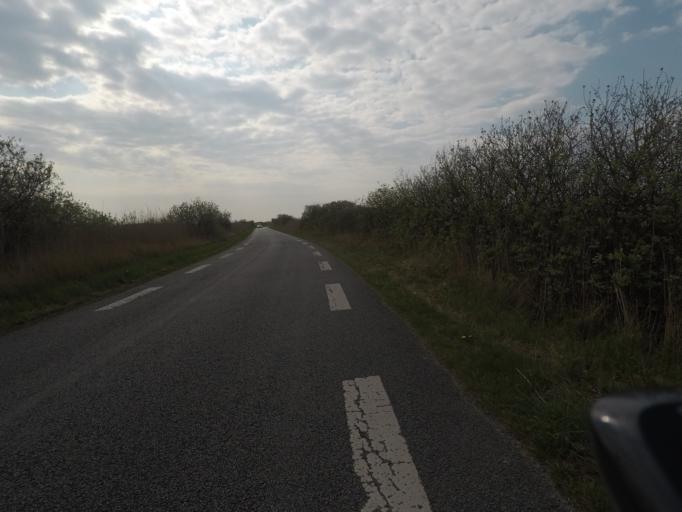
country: DE
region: Schleswig-Holstein
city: List
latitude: 55.1313
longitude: 8.5102
